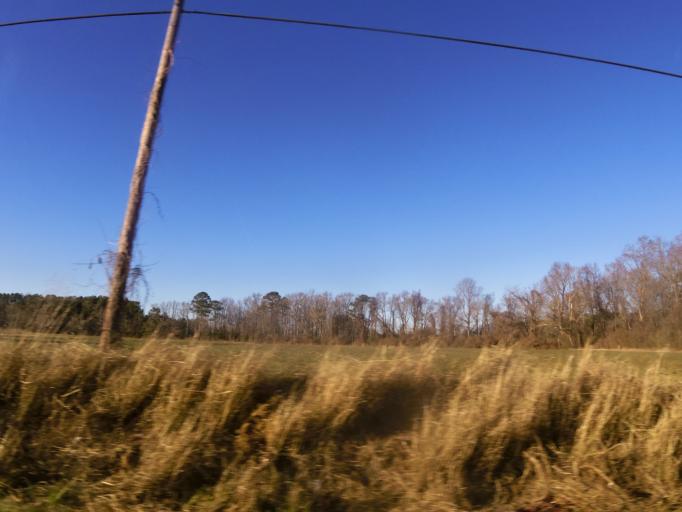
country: US
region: Virginia
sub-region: Isle of Wight County
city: Windsor
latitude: 36.6901
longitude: -76.7502
